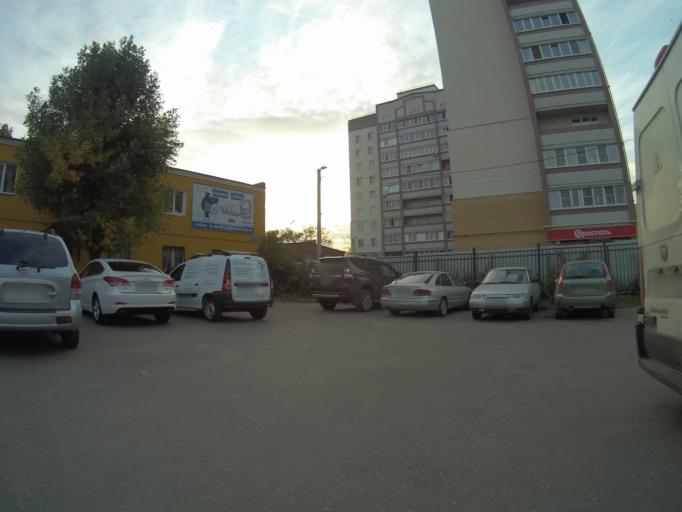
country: RU
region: Vladimir
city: Vladimir
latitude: 56.1421
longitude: 40.3817
